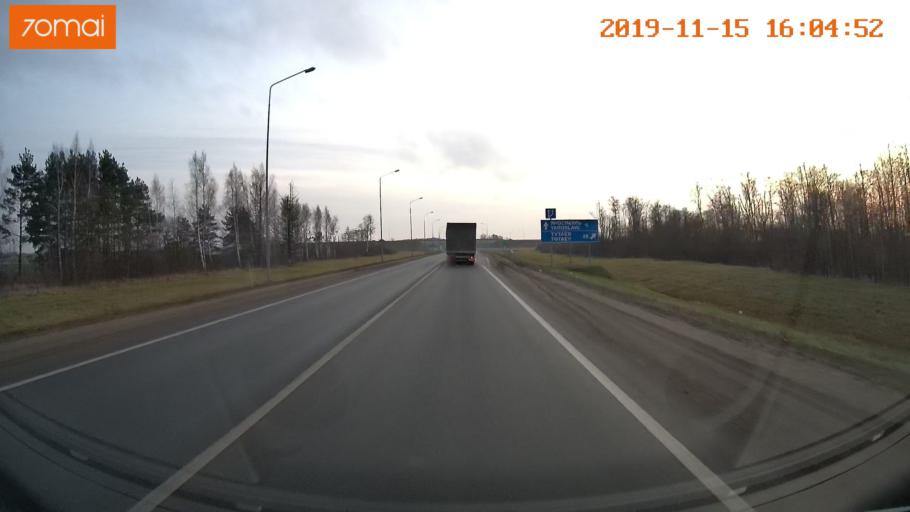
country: RU
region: Jaroslavl
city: Yaroslavl
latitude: 57.7428
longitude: 39.8979
